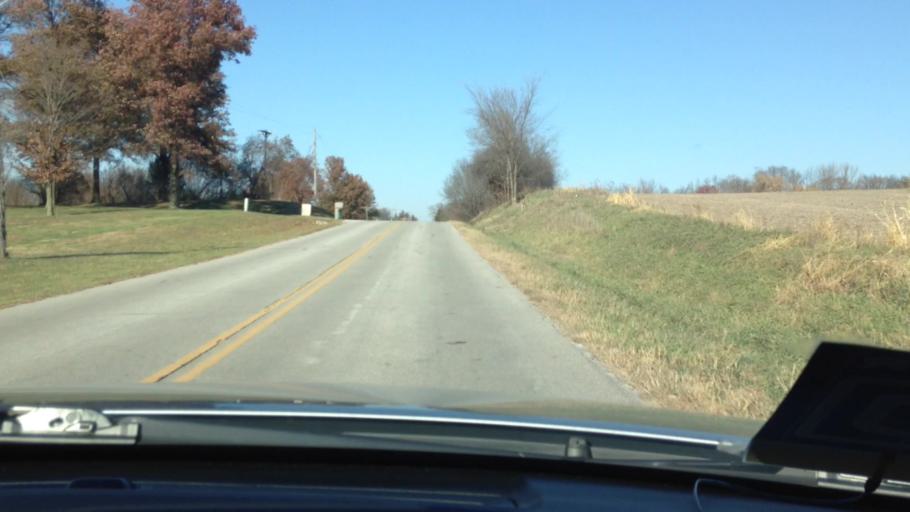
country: US
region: Missouri
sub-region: Platte County
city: Weston
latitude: 39.4336
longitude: -94.8541
